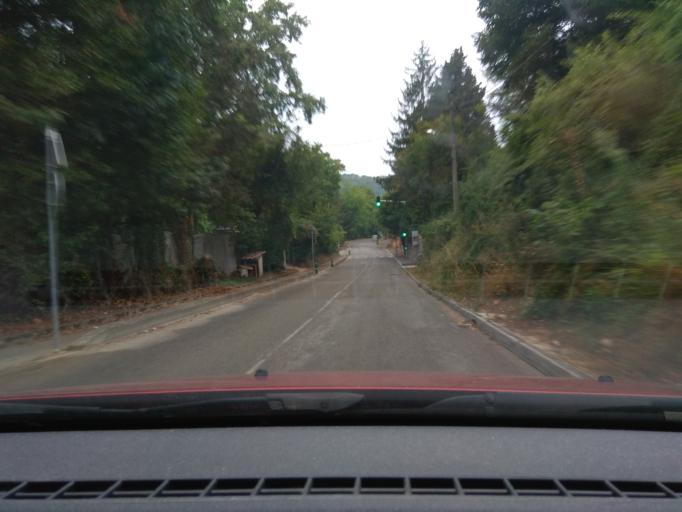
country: FR
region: Provence-Alpes-Cote d'Azur
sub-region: Departement des Alpes-Maritimes
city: La Colle-sur-Loup
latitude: 43.6834
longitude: 7.0920
